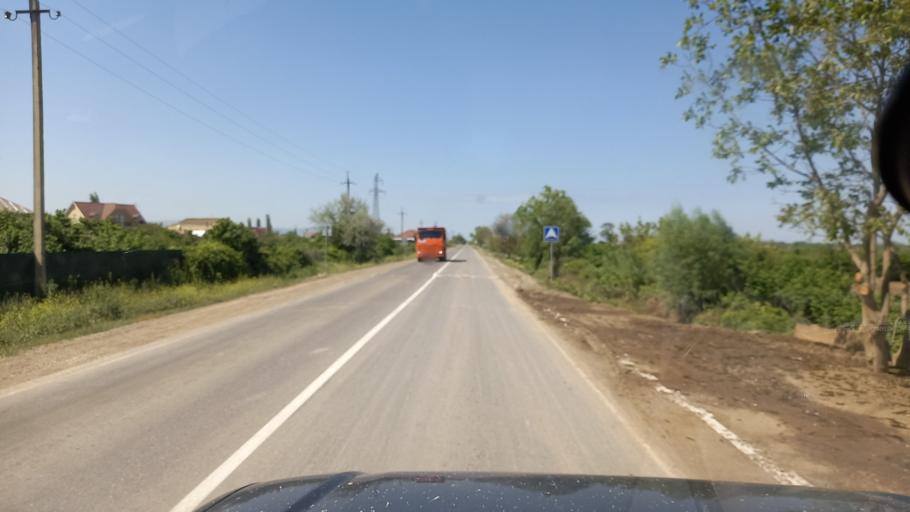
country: RU
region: Dagestan
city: Novaya Maka
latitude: 41.8206
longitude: 48.4011
